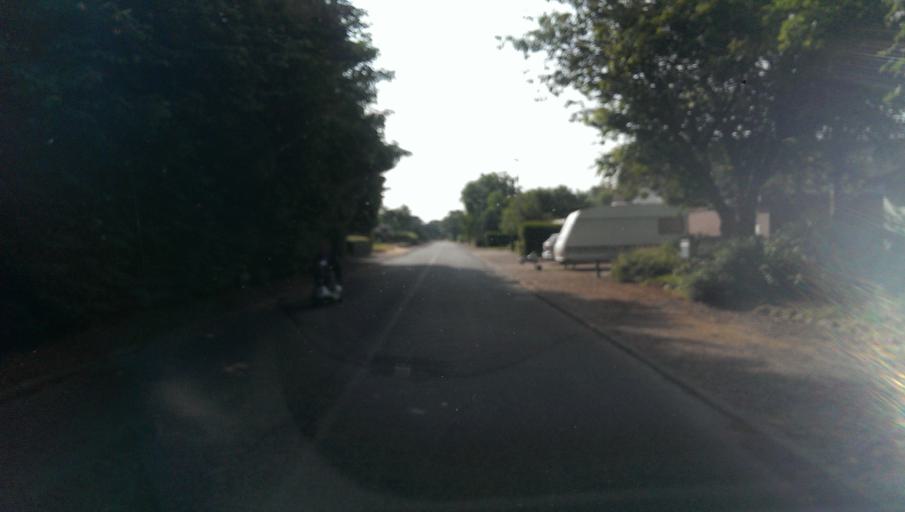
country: DK
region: South Denmark
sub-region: Esbjerg Kommune
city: Tjaereborg
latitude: 55.4325
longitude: 8.6389
